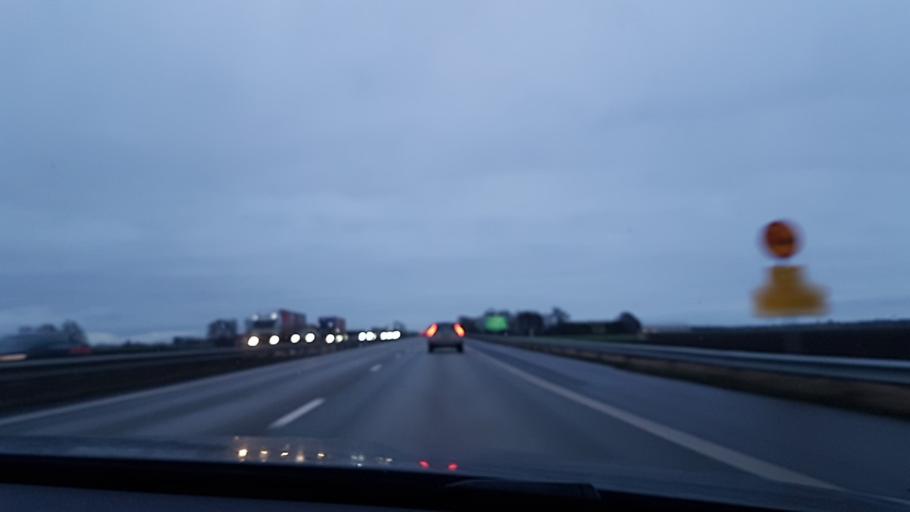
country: SE
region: Skane
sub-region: Lomma Kommun
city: Lomma
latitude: 55.7172
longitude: 13.0923
